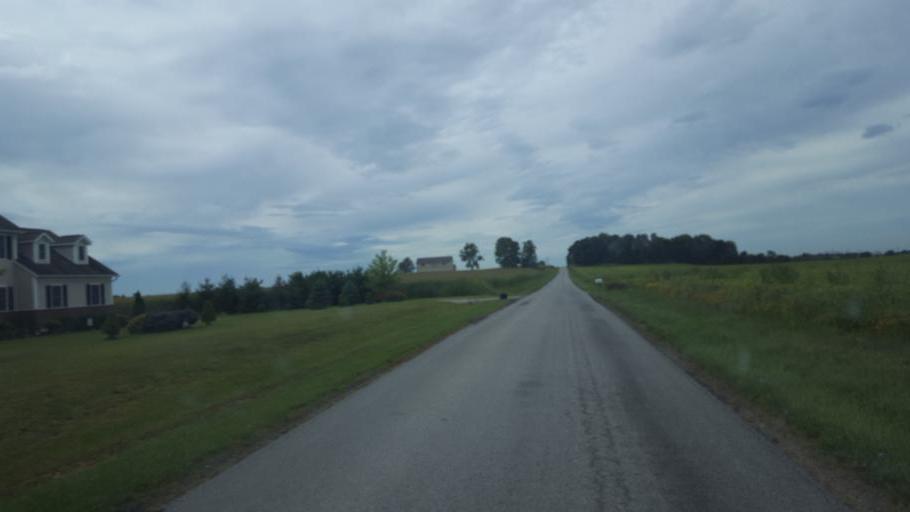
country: US
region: Ohio
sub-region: Knox County
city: Centerburg
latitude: 40.2596
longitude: -82.7195
